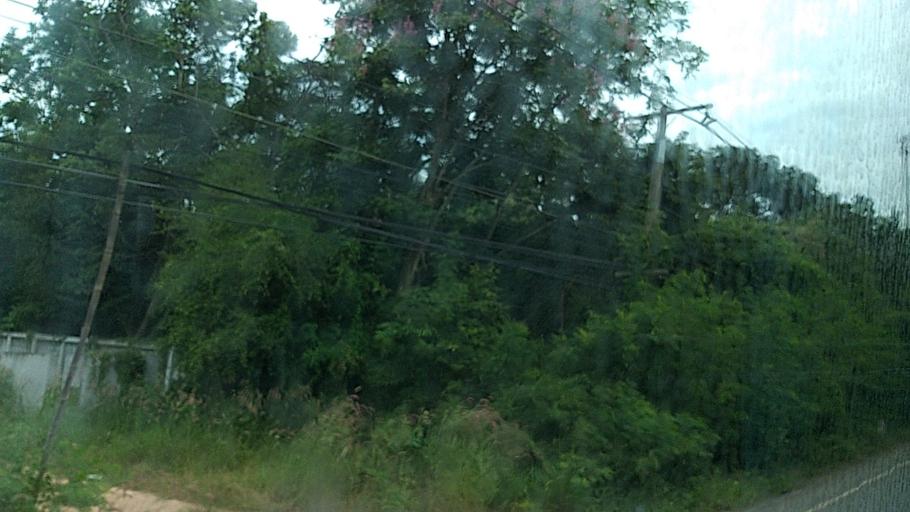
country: TH
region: Maha Sarakham
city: Kantharawichai
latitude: 16.3278
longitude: 103.2859
